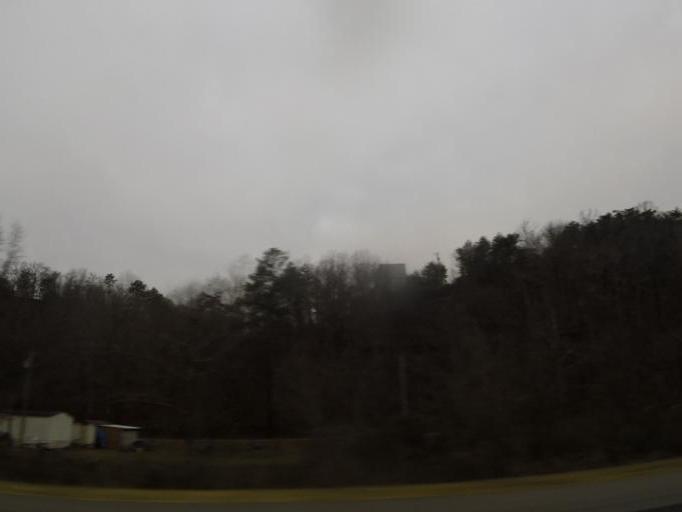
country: US
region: Alabama
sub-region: Cullman County
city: Good Hope
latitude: 34.0323
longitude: -86.8717
